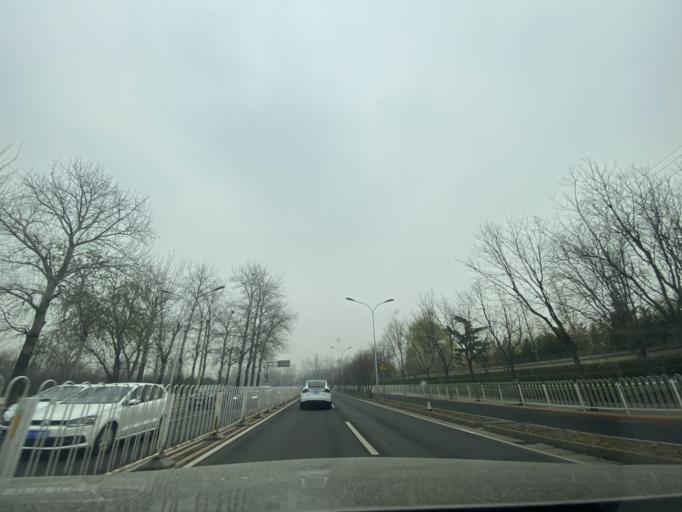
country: CN
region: Beijing
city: Sijiqing
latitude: 39.9701
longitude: 116.2582
